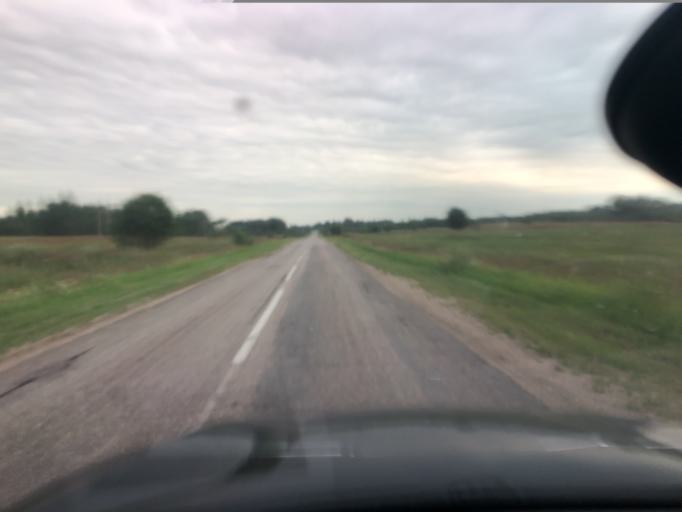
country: RU
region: Jaroslavl
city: Petrovsk
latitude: 57.0022
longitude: 39.0317
